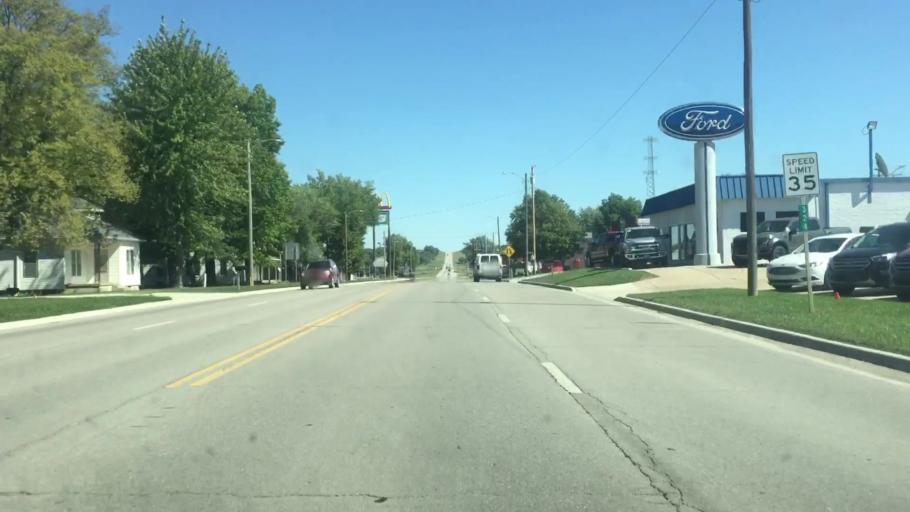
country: US
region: Kansas
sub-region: Nemaha County
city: Seneca
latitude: 39.8413
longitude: -96.0599
